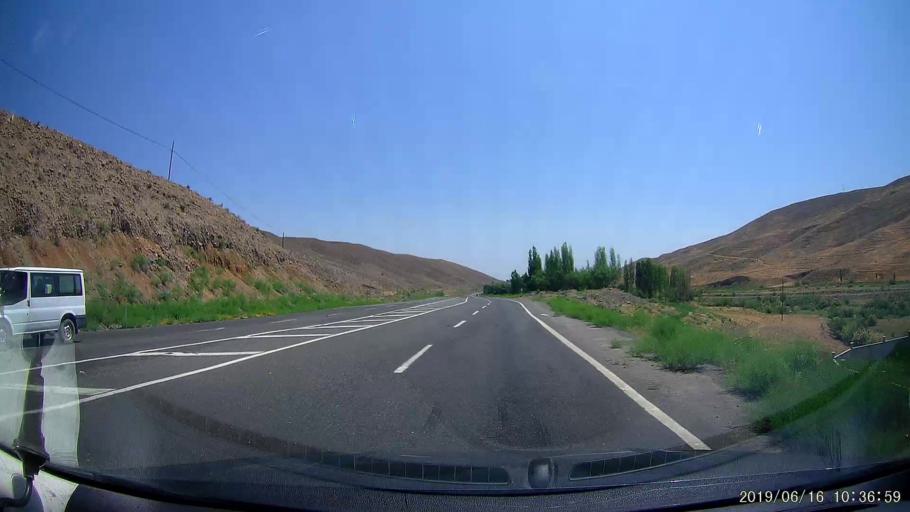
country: TR
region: Igdir
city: Tuzluca
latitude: 40.0435
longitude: 43.6901
